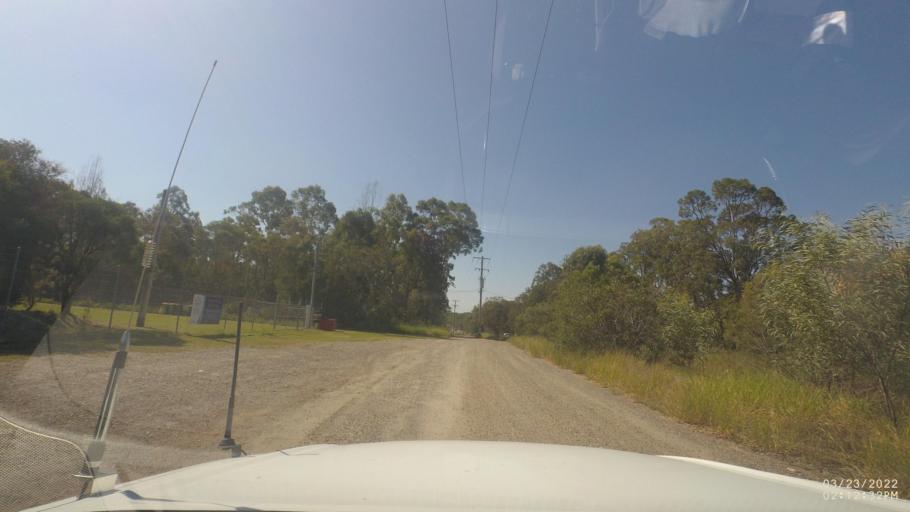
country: AU
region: Queensland
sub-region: Logan
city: Logan Reserve
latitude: -27.7415
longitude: 153.1255
